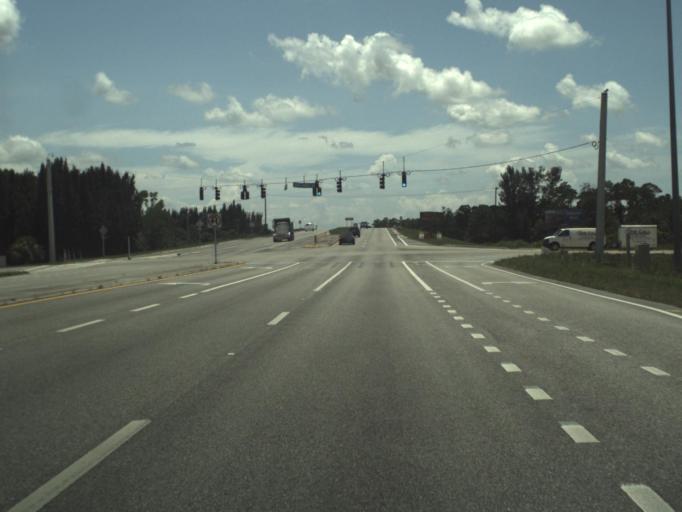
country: US
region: Florida
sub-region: Martin County
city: Palm City
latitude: 27.1071
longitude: -80.2628
